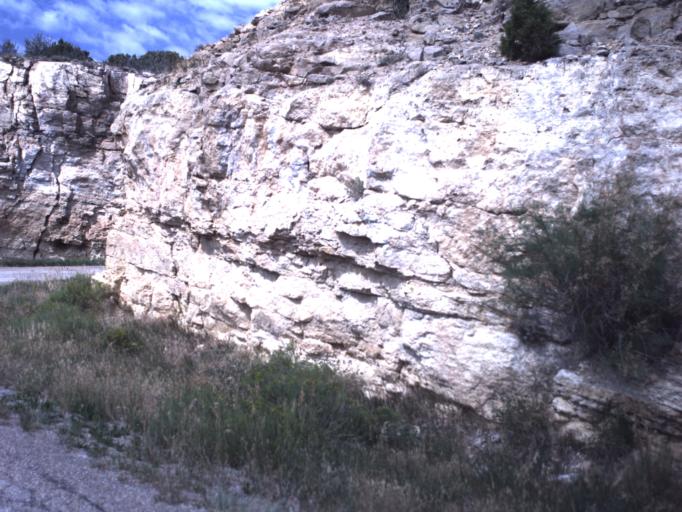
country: US
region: Utah
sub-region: Daggett County
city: Manila
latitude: 40.9071
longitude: -109.6988
